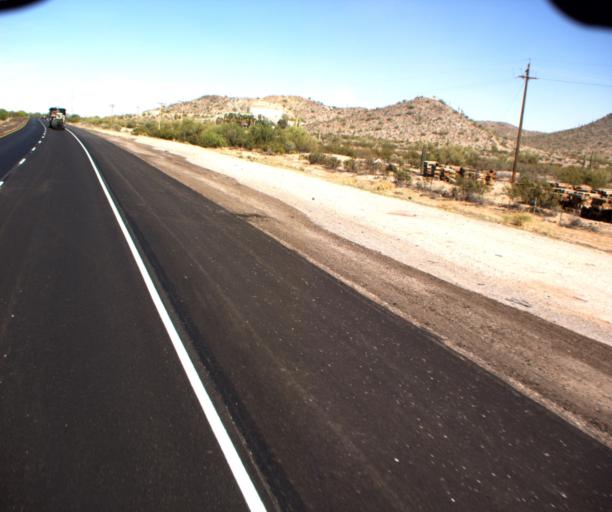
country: US
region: Arizona
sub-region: Pinal County
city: Casa Grande
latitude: 32.8310
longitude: -111.7322
